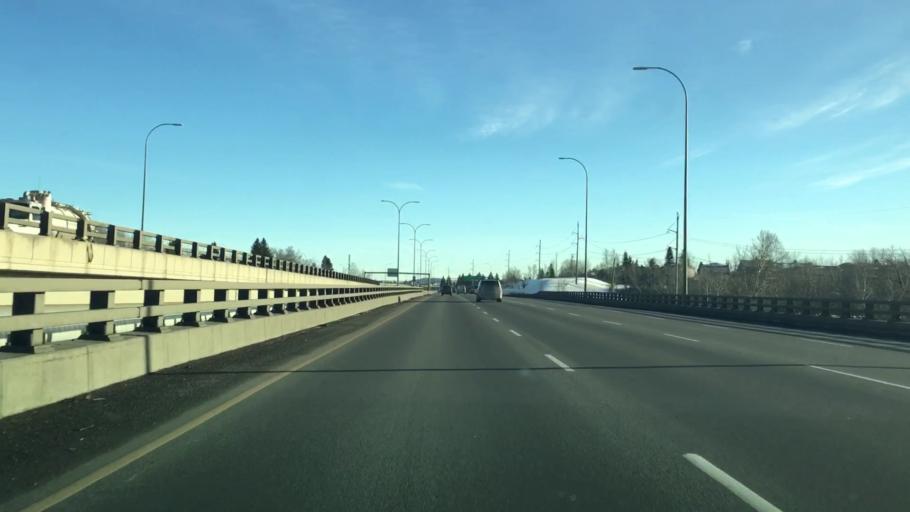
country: CA
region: Alberta
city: Calgary
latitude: 50.9868
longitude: -114.0250
